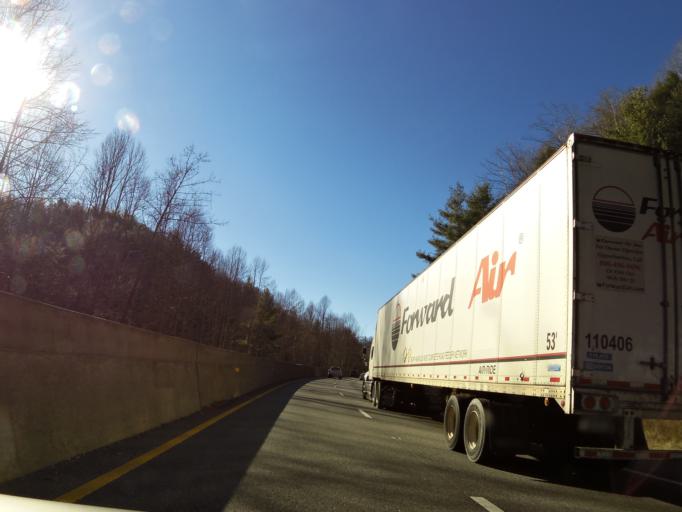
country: US
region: North Carolina
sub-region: Haywood County
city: Cove Creek
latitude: 35.6588
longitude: -82.9902
